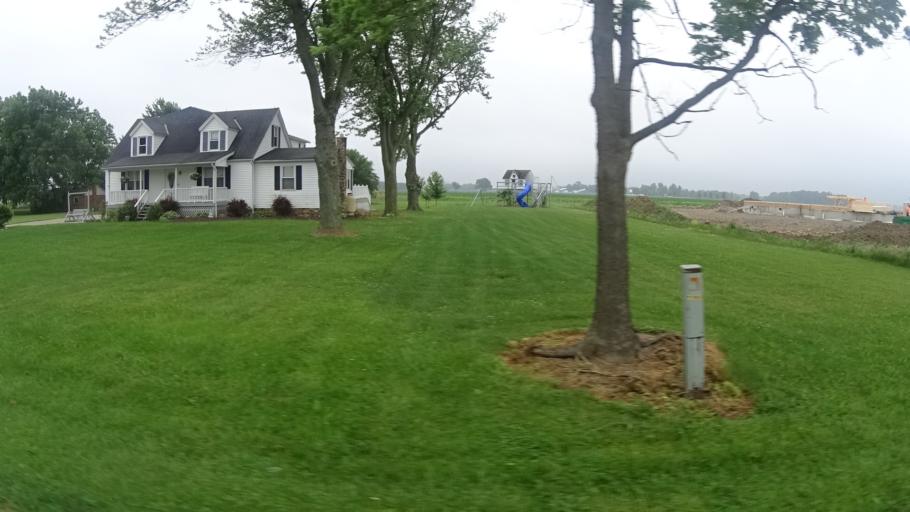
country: US
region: Ohio
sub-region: Huron County
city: Bellevue
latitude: 41.3617
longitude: -82.7823
